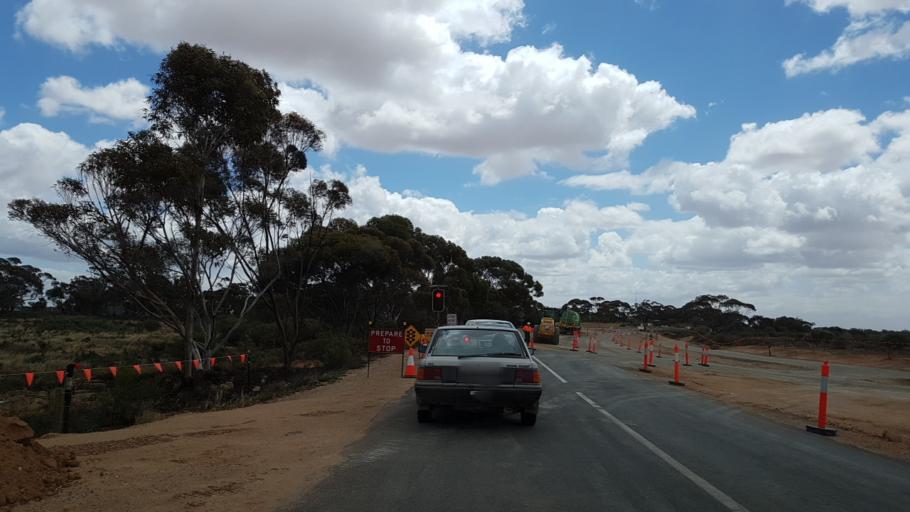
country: AU
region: South Australia
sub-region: Loxton Waikerie
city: Waikerie
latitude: -34.1883
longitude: 140.0172
